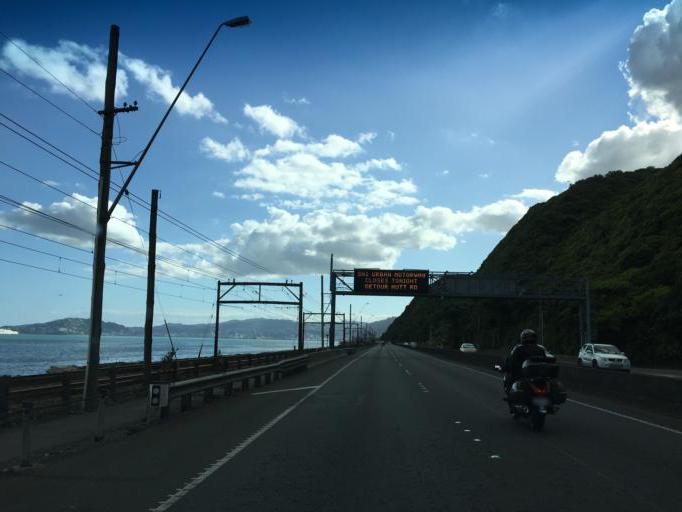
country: NZ
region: Wellington
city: Petone
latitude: -41.2362
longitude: 174.8325
